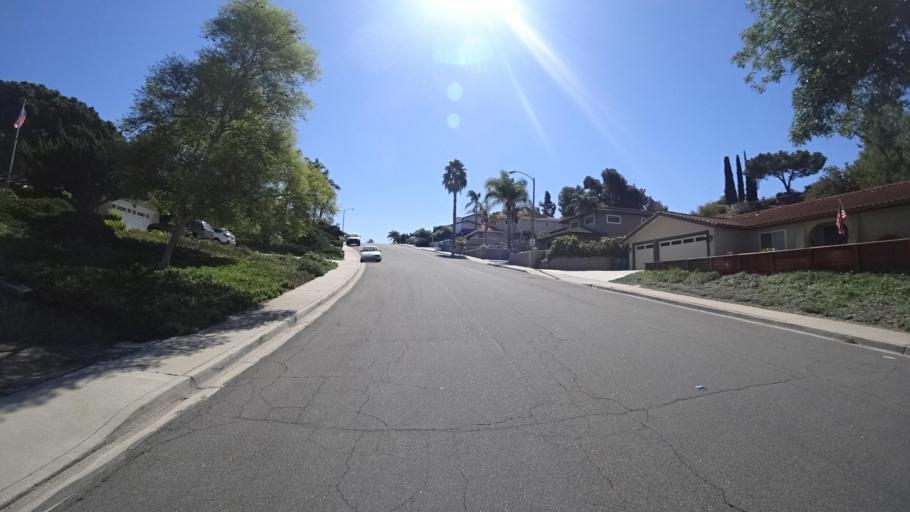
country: US
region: California
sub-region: San Diego County
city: Bonita
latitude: 32.6675
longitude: -117.0175
